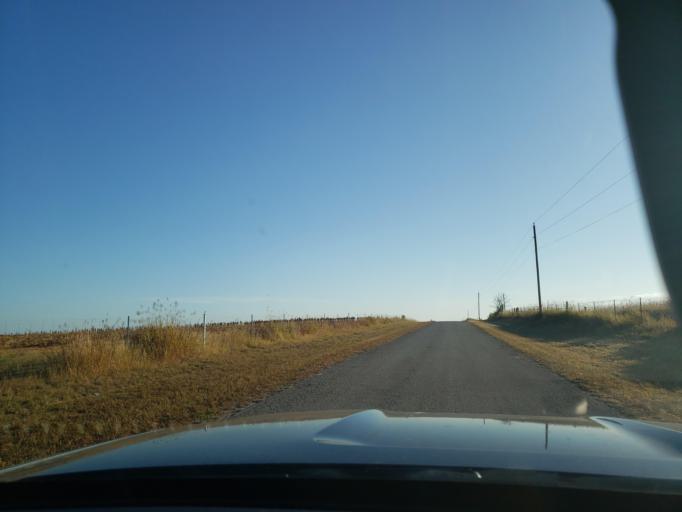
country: US
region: Texas
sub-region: Bee County
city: Beeville
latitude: 28.4257
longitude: -97.7010
